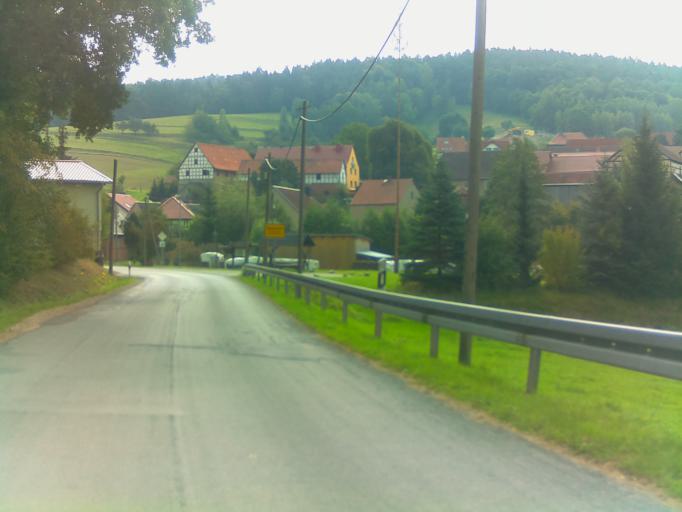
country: DE
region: Thuringia
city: Schops
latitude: 50.8264
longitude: 11.6057
